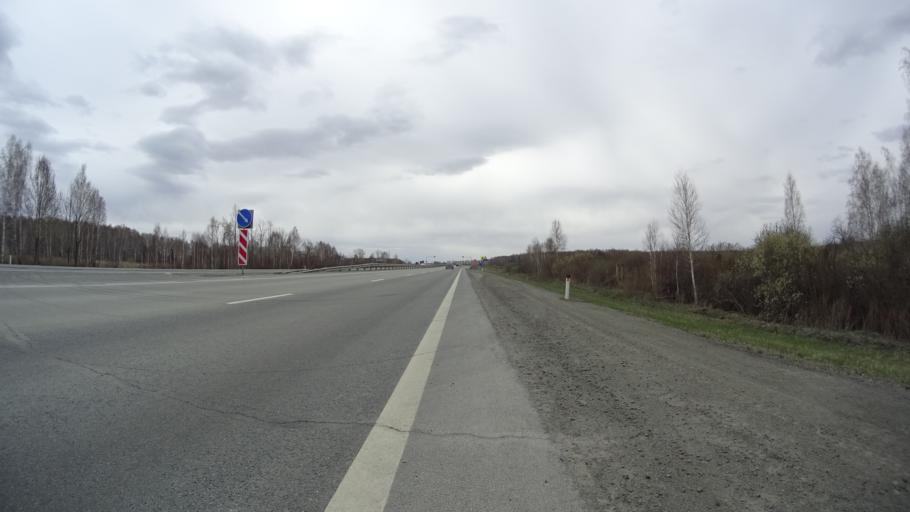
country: RU
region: Chelyabinsk
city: Yemanzhelinka
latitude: 54.8265
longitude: 61.3103
